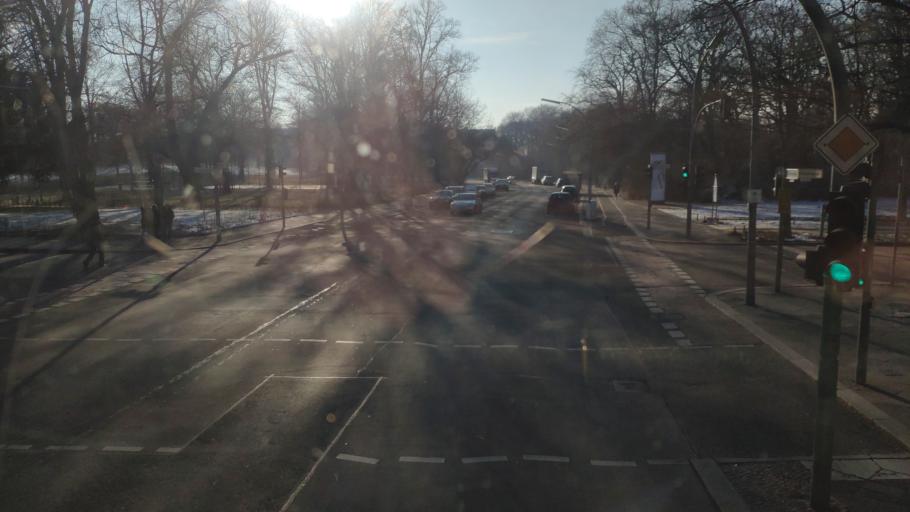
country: DE
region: Berlin
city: Wedding Bezirk
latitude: 52.5585
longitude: 13.3513
